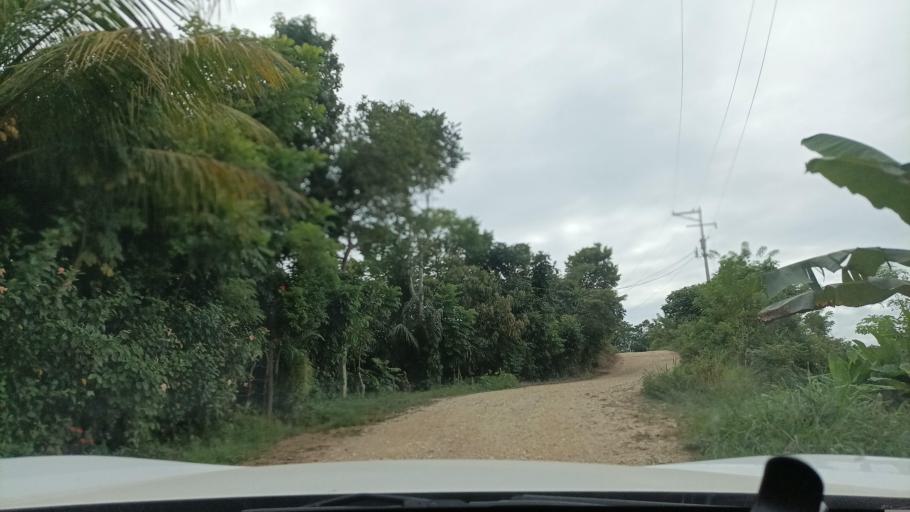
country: MX
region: Veracruz
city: Hidalgotitlan
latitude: 17.6061
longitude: -94.4289
